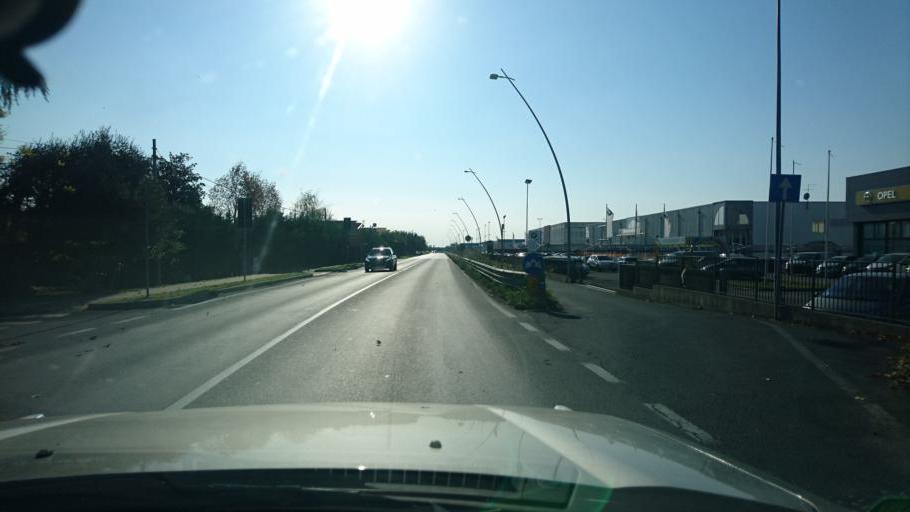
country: IT
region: Veneto
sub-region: Provincia di Padova
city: Monselice
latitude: 45.2170
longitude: 11.7552
